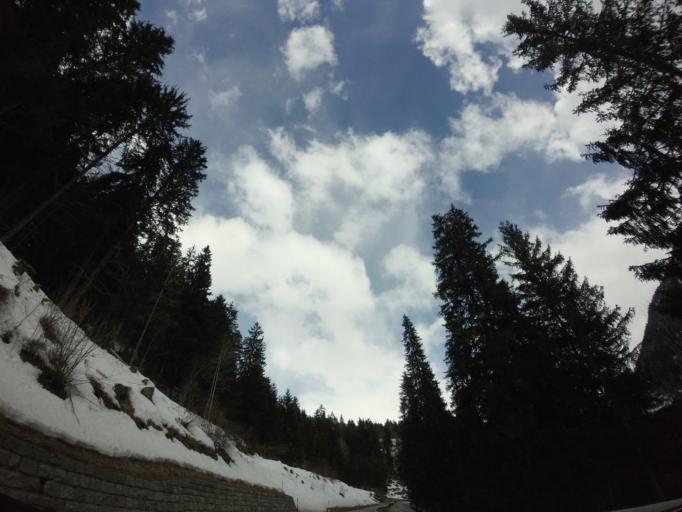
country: AT
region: Tyrol
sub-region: Politischer Bezirk Landeck
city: Nauders
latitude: 46.8429
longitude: 10.4172
